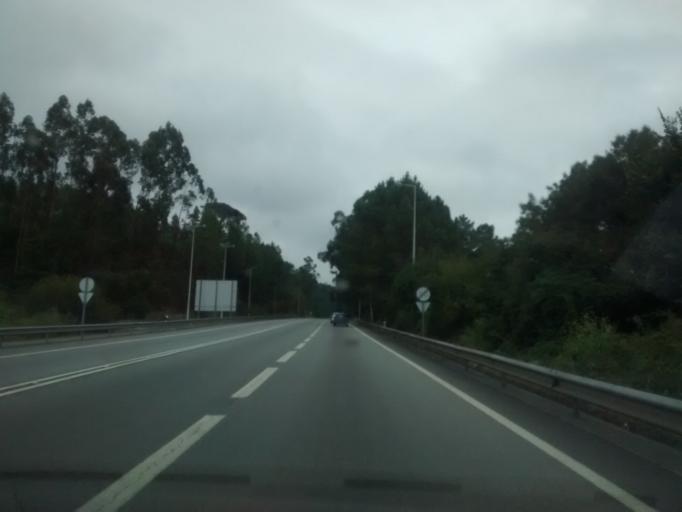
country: PT
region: Braga
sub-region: Braga
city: Oliveira
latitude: 41.5052
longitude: -8.4548
